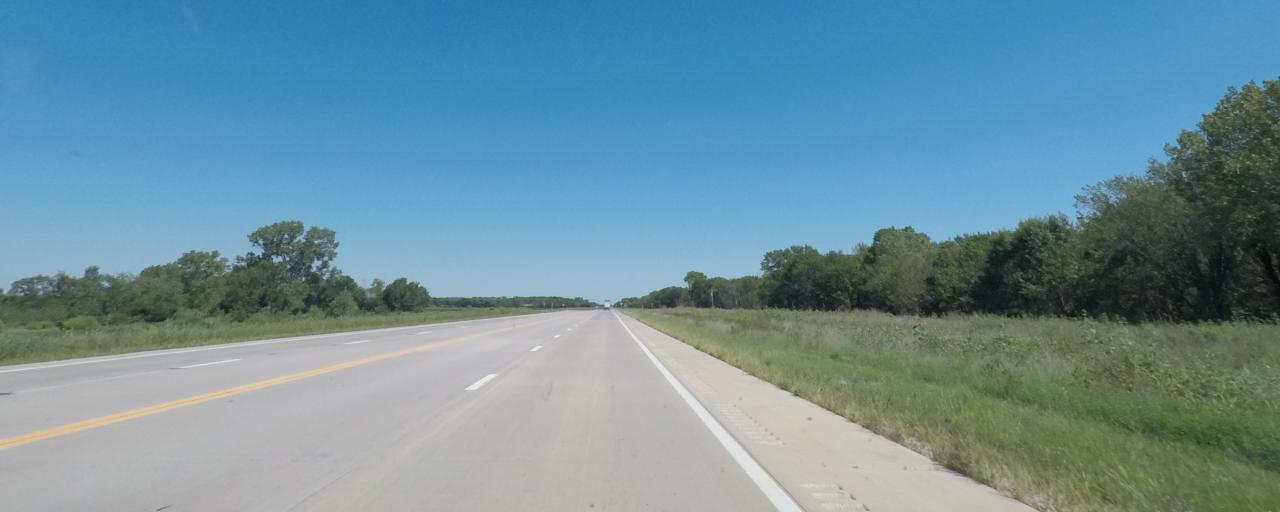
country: US
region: Kansas
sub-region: Lyon County
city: Emporia
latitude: 38.4067
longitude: -96.3579
